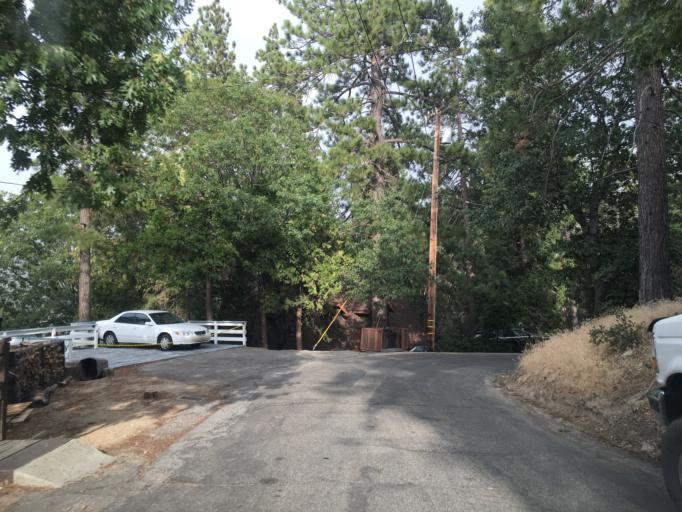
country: US
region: California
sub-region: San Bernardino County
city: Crestline
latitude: 34.2513
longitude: -117.2739
